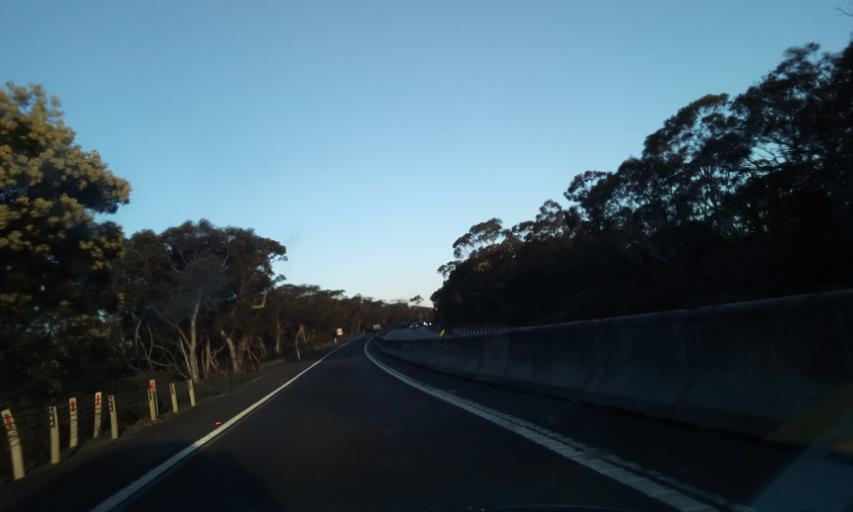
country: AU
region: New South Wales
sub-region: Wollongong
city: Mount Keira
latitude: -34.3214
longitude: 150.7646
